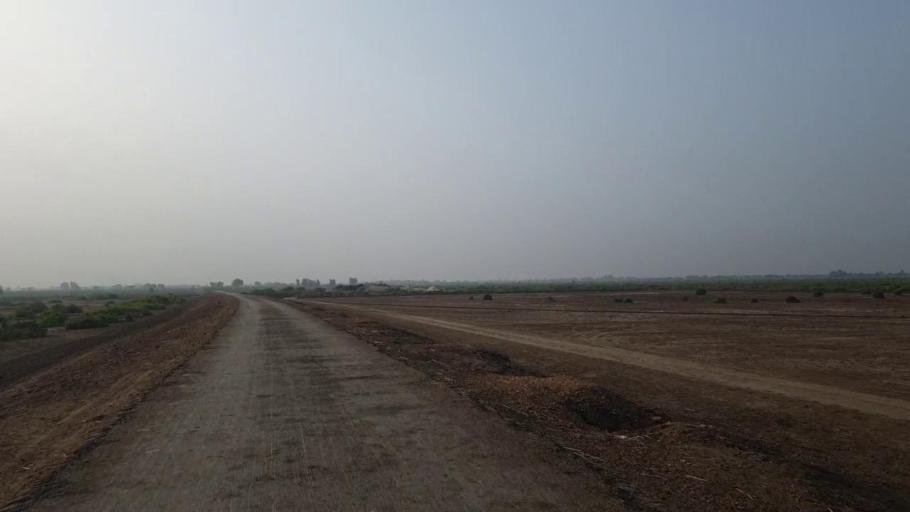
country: PK
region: Sindh
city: Tando Muhammad Khan
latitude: 25.1597
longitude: 68.6098
